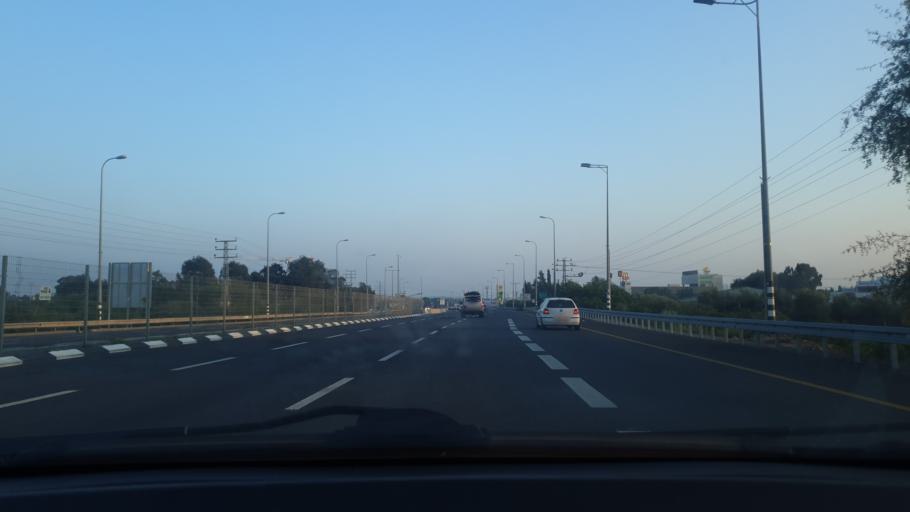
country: IL
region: Central District
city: Kefar Habad
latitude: 31.9723
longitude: 34.8414
